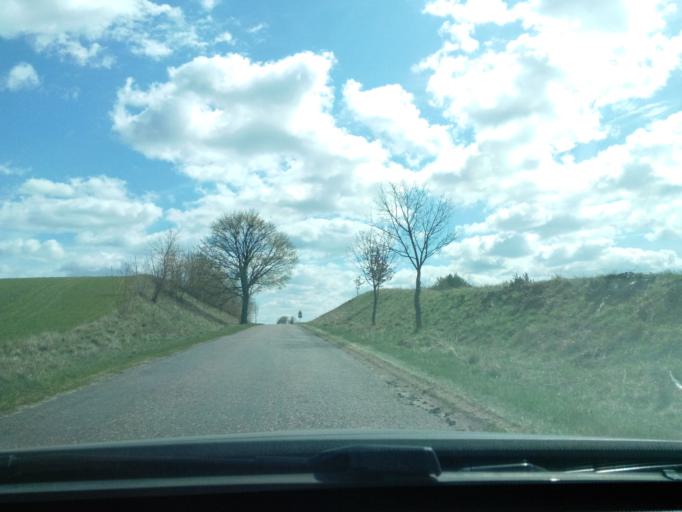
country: PL
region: Warmian-Masurian Voivodeship
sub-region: Powiat nowomiejski
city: Biskupiec
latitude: 53.4660
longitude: 19.2665
